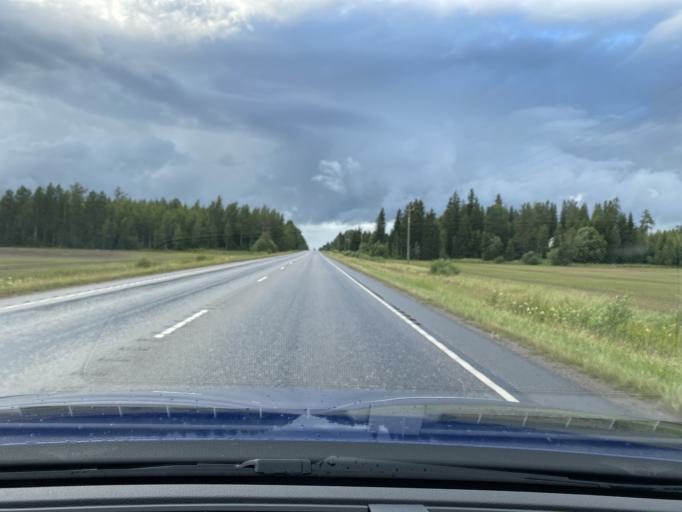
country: FI
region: Uusimaa
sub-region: Helsinki
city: Nurmijaervi
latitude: 60.5390
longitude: 24.8357
